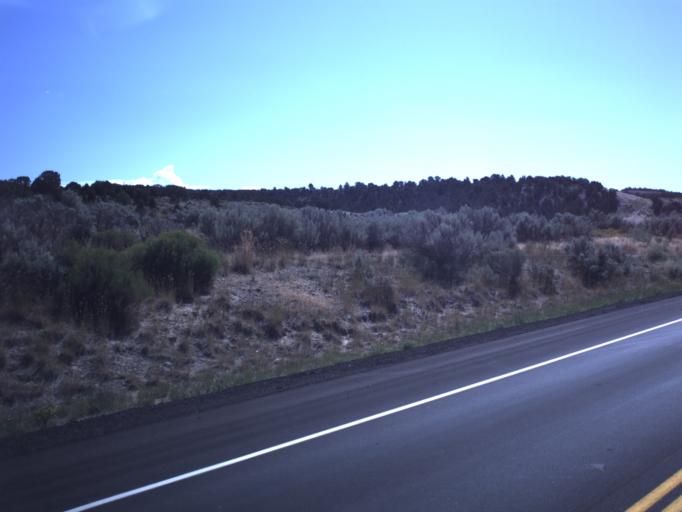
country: US
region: Utah
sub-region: Utah County
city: Eagle Mountain
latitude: 39.9903
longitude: -112.2672
